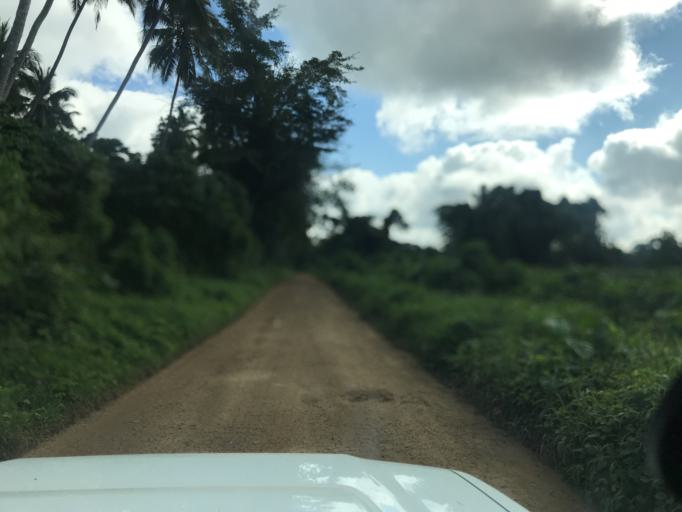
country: VU
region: Sanma
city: Luganville
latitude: -15.4942
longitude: 167.0895
